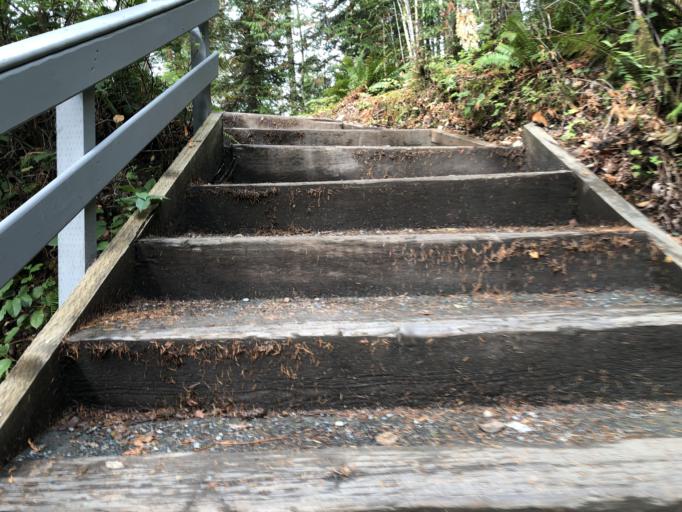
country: CA
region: British Columbia
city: Sooke
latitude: 48.4378
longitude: -123.7174
